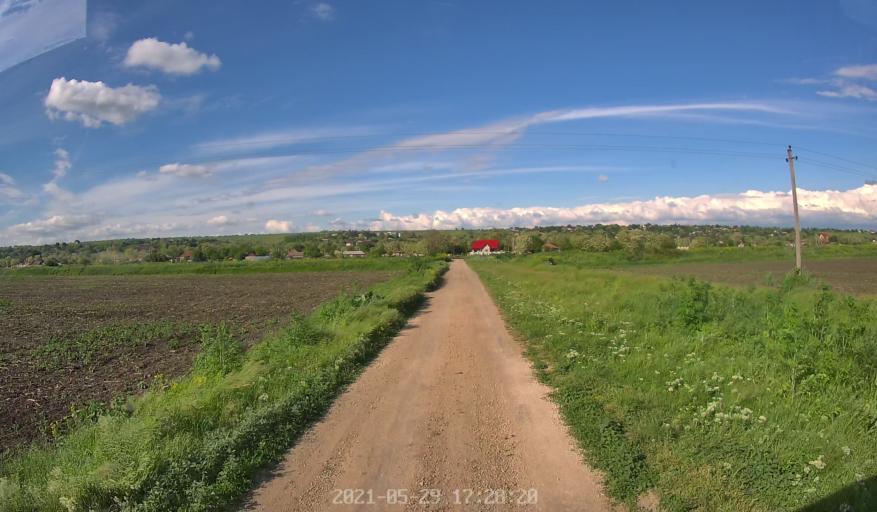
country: MD
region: Laloveni
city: Ialoveni
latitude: 46.8333
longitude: 28.8405
